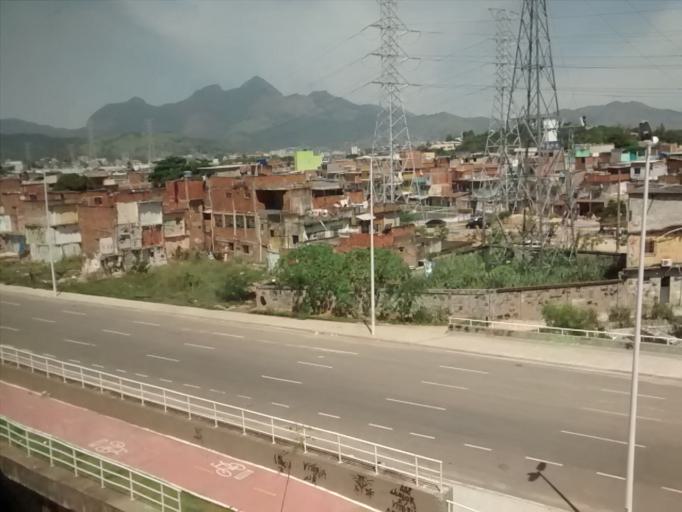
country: BR
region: Rio de Janeiro
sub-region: Rio De Janeiro
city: Rio de Janeiro
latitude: -22.8788
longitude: -43.2513
